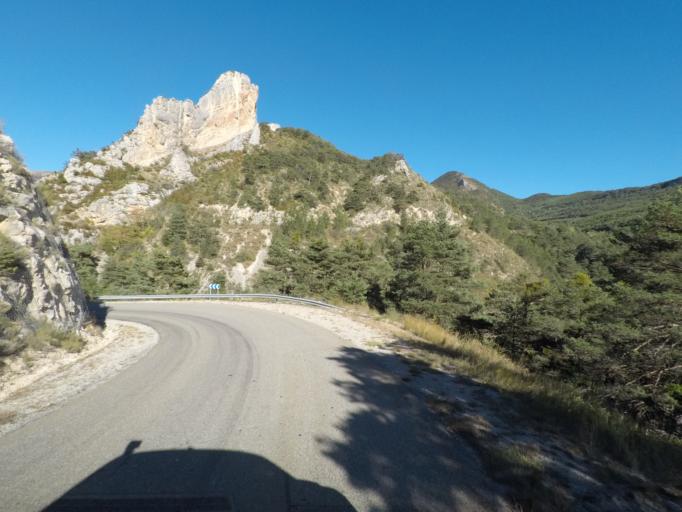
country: FR
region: Provence-Alpes-Cote d'Azur
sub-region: Departement des Hautes-Alpes
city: Serres
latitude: 44.4367
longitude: 5.5585
